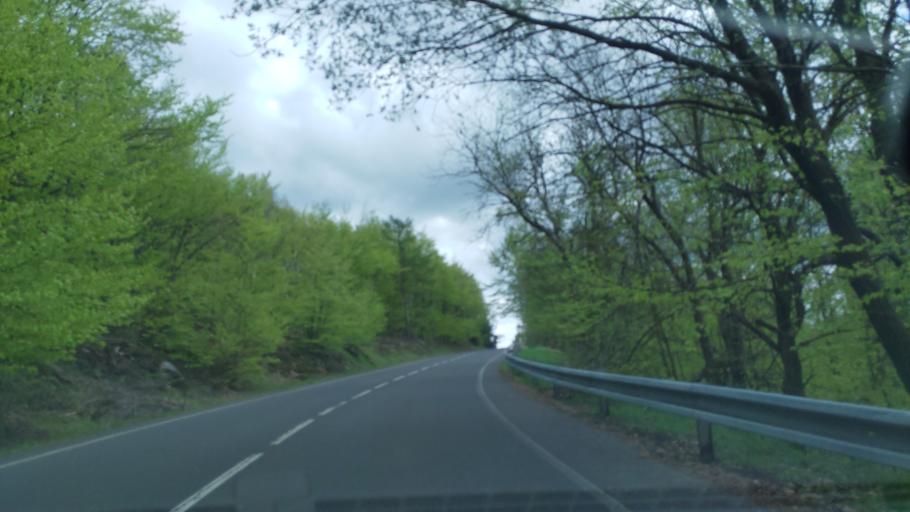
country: CZ
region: Ustecky
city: Libouchec
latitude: 50.7874
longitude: 14.0409
